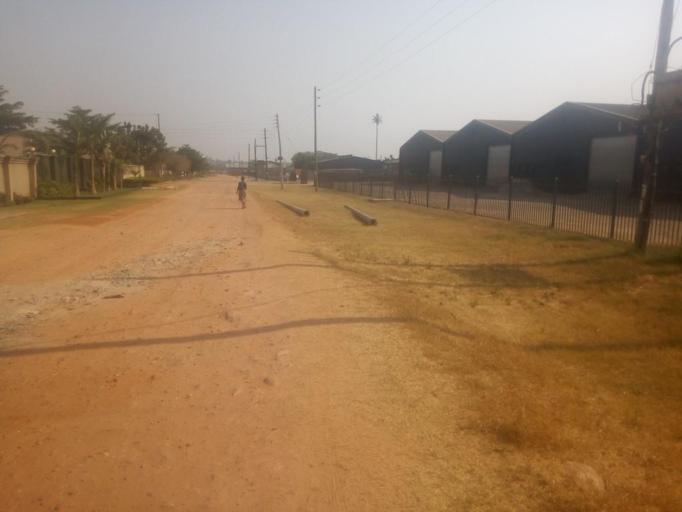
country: ZM
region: Lusaka
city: Lusaka
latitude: -15.3973
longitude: 28.3939
